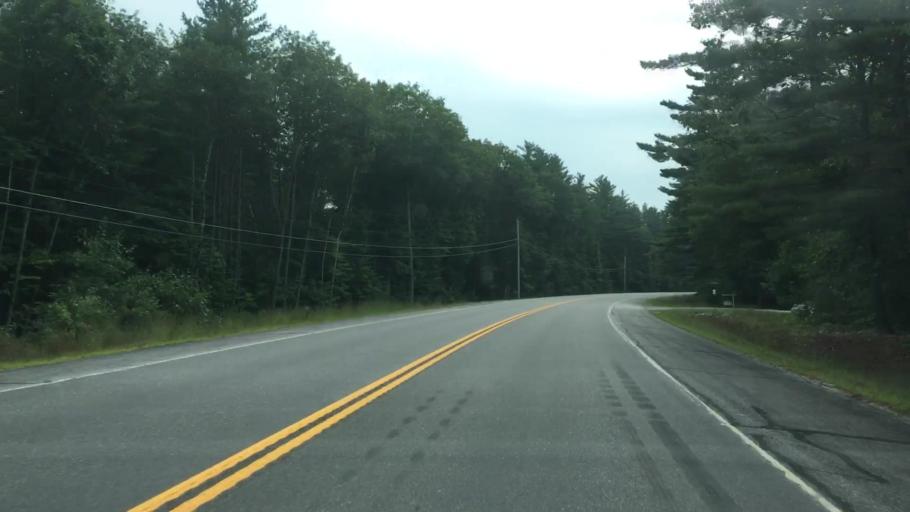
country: US
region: Maine
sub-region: Oxford County
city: Bethel
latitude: 44.4880
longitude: -70.6997
